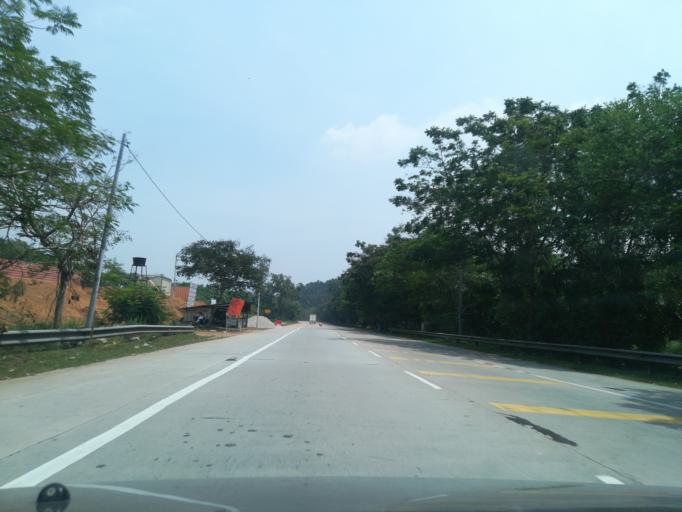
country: MY
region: Kedah
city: Kulim
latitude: 5.4256
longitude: 100.5647
